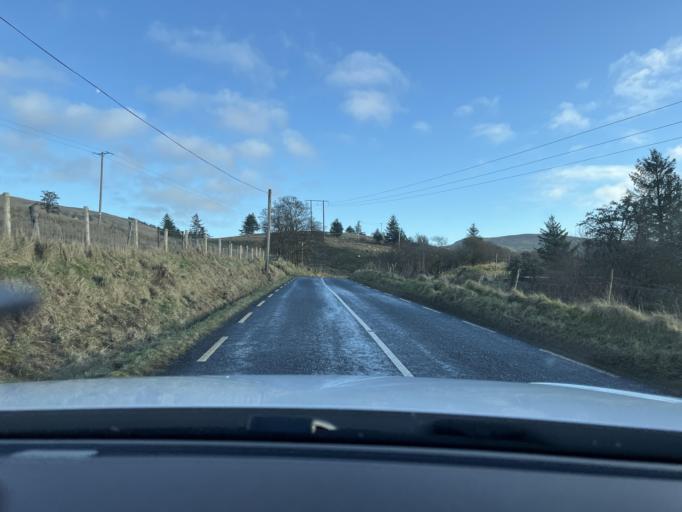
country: GB
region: Northern Ireland
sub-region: Fermanagh District
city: Enniskillen
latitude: 54.1770
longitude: -7.8527
